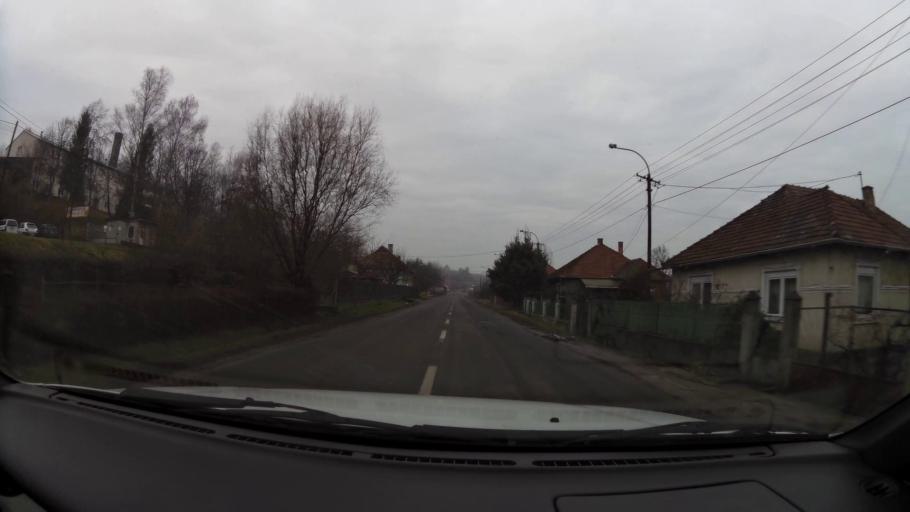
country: HU
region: Borsod-Abauj-Zemplen
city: Izsofalva
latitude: 48.3160
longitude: 20.6513
